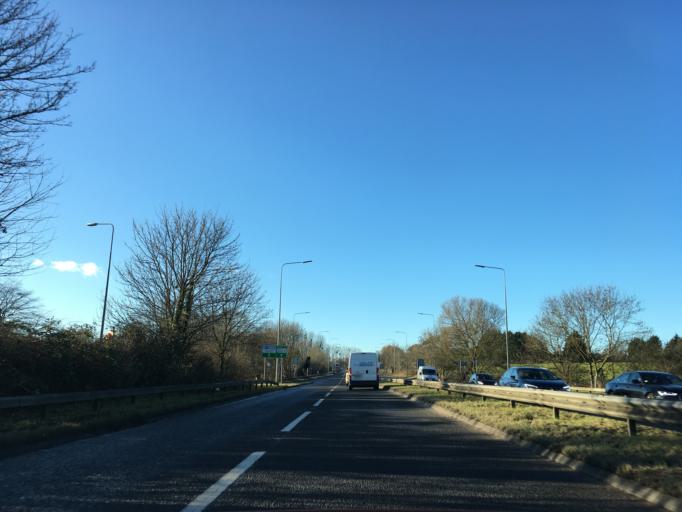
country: GB
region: England
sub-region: Bath and North East Somerset
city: Keynsham
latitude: 51.4256
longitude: -2.5199
